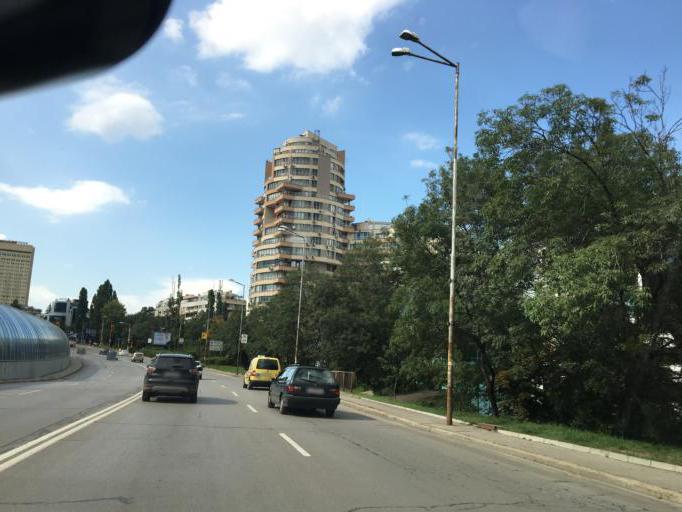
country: BG
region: Sofia-Capital
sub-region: Stolichna Obshtina
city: Sofia
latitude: 42.6697
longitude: 23.3523
